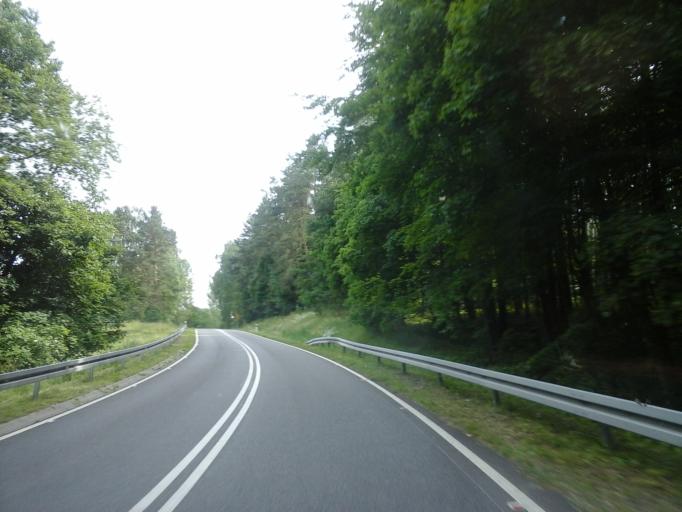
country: PL
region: West Pomeranian Voivodeship
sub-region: Powiat stargardzki
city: Insko
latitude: 53.4761
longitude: 15.5779
